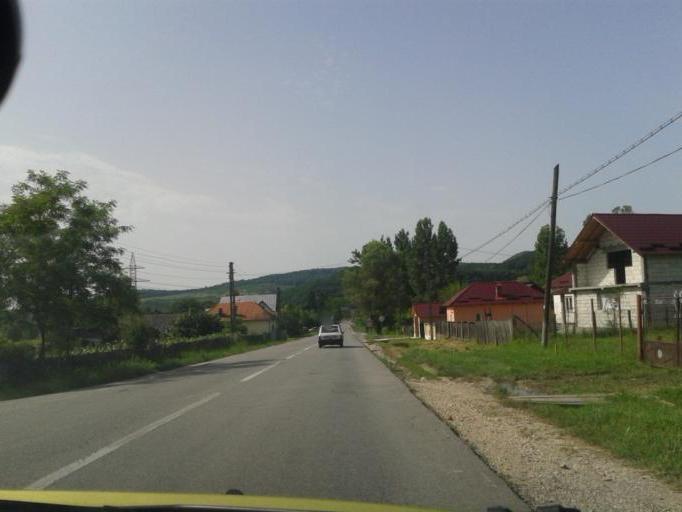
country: RO
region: Valcea
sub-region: Oras Baile Govora
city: Baile Govora
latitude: 45.0789
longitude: 24.2187
